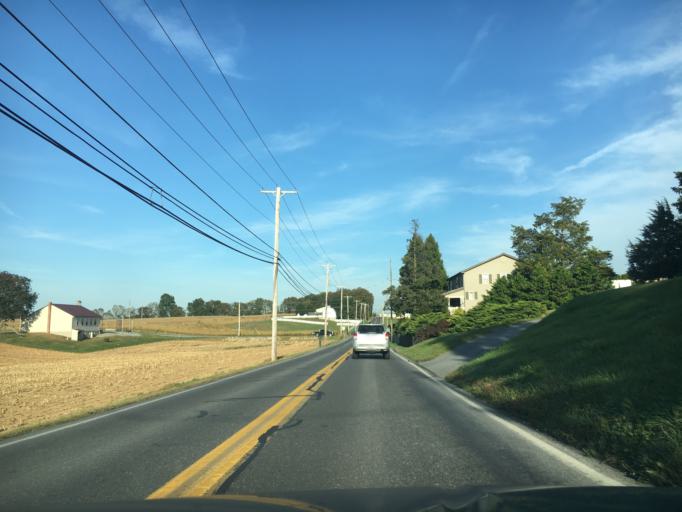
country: US
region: Pennsylvania
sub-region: Lancaster County
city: Ephrata
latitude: 40.1338
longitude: -76.1379
